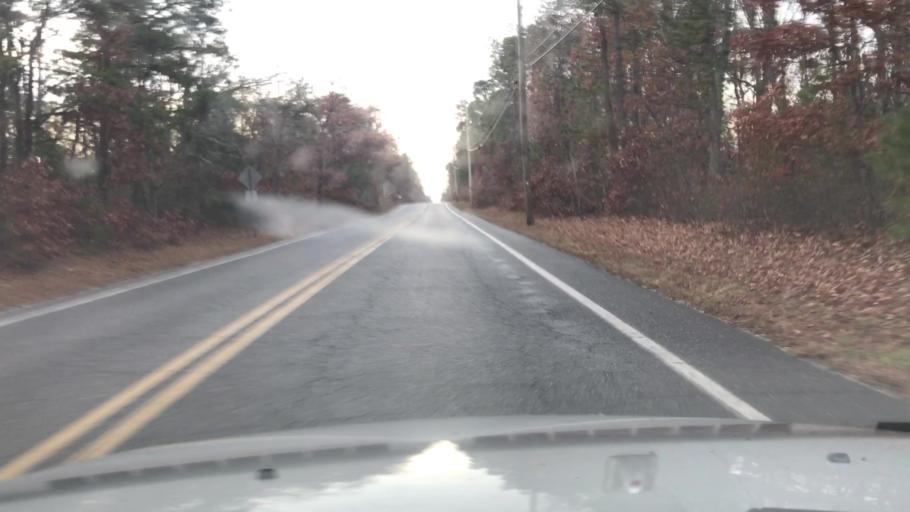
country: US
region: New Jersey
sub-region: Cape May County
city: Sea Isle City
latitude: 39.1912
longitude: -74.7570
